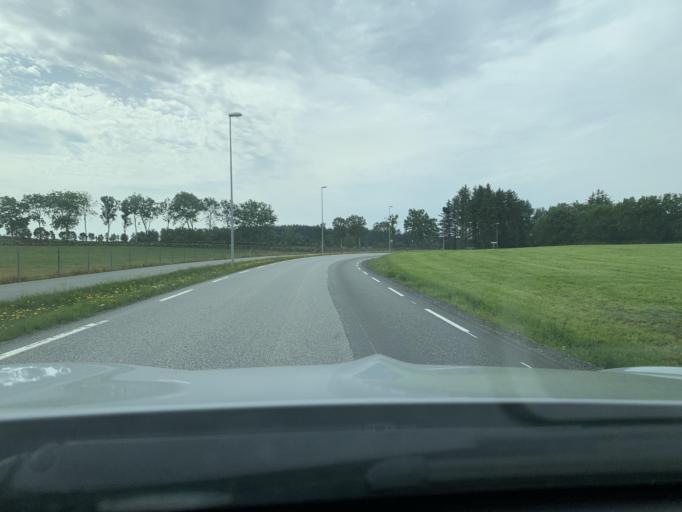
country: NO
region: Rogaland
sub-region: Time
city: Bryne
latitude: 58.7570
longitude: 5.7087
